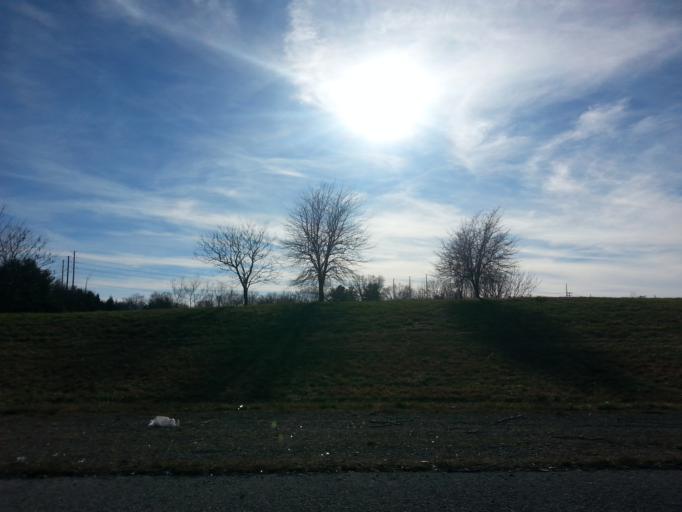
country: US
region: Tennessee
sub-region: Warren County
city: McMinnville
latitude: 35.6947
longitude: -85.8037
